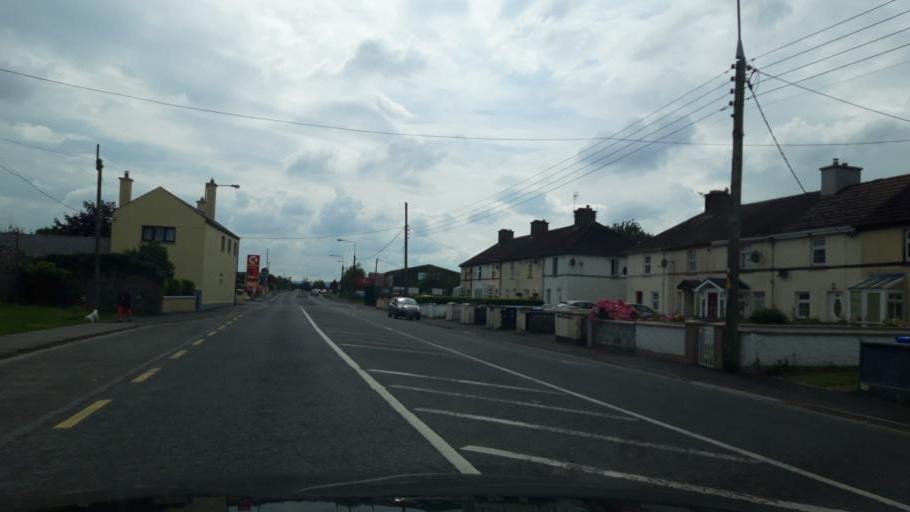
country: IE
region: Leinster
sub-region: Kildare
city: Athy
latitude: 52.9876
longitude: -6.9956
